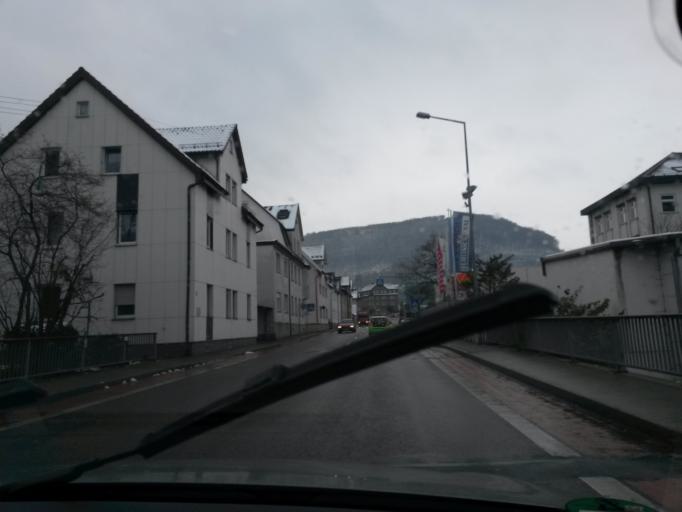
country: DE
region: Baden-Wuerttemberg
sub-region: Regierungsbezirk Stuttgart
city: Geislingen an der Steige
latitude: 48.6254
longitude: 9.8369
